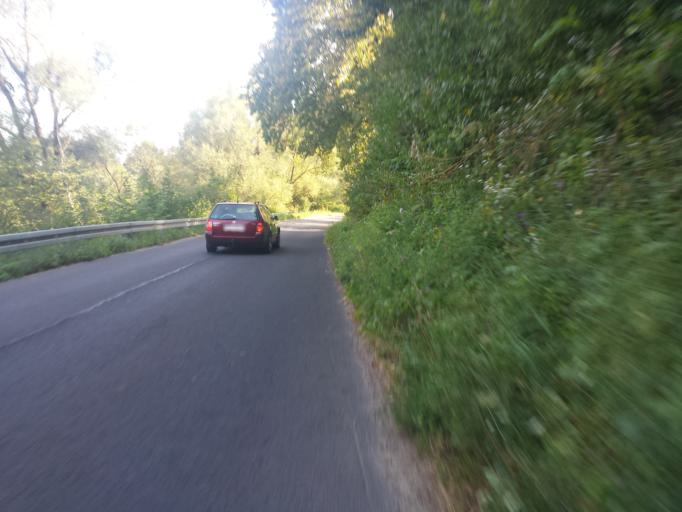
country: PL
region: Subcarpathian Voivodeship
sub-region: Powiat leski
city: Uherce Mineralne
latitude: 49.4595
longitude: 22.3963
